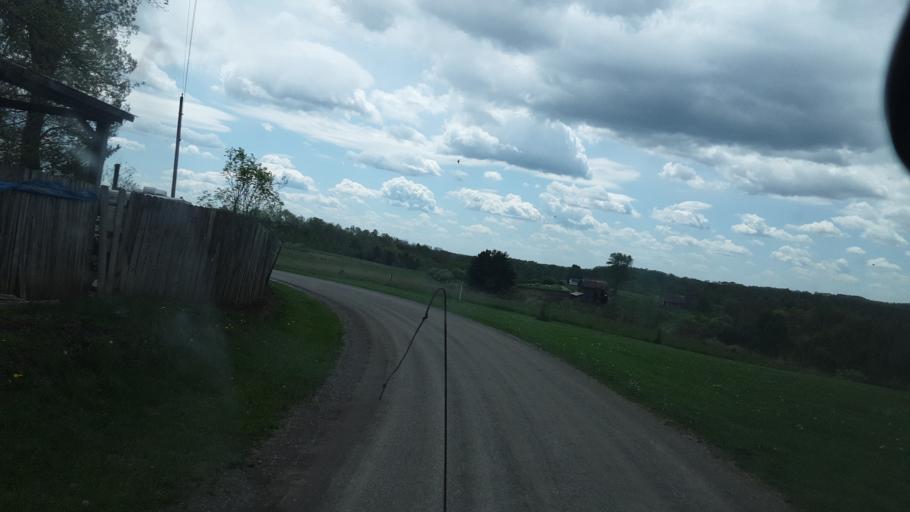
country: US
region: Ohio
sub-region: Noble County
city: Caldwell
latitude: 39.7600
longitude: -81.6236
